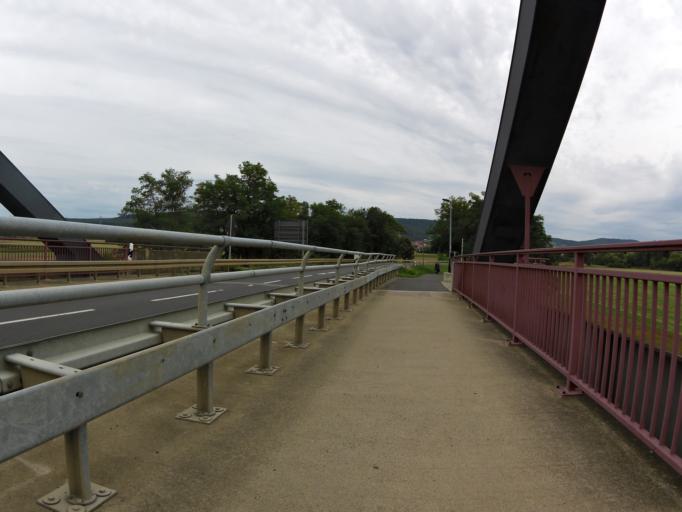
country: DE
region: Bavaria
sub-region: Regierungsbezirk Unterfranken
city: Zeil
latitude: 50.0019
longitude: 10.5918
